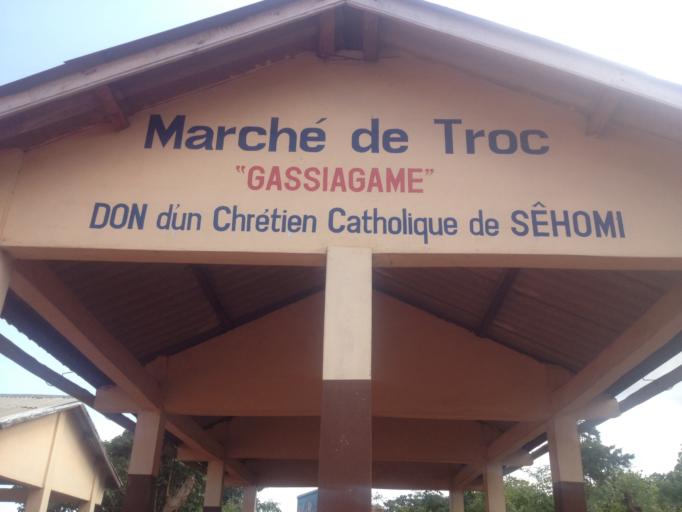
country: BJ
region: Mono
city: Come
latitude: 6.5078
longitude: 1.9629
